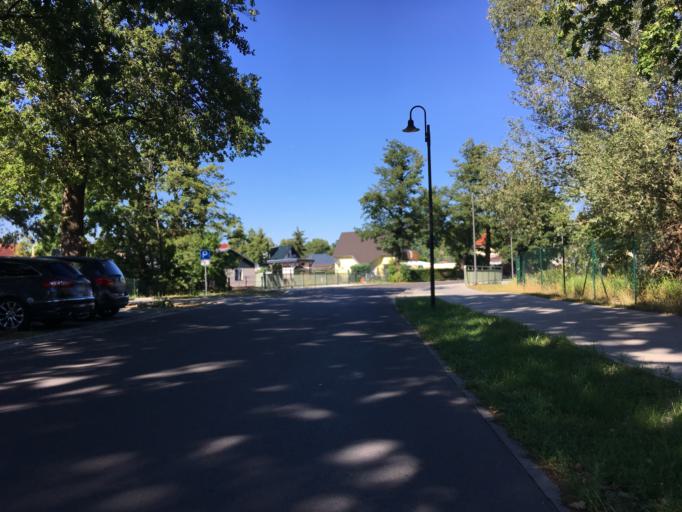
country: DE
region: Brandenburg
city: Schulzendorf
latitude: 52.3674
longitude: 13.5937
